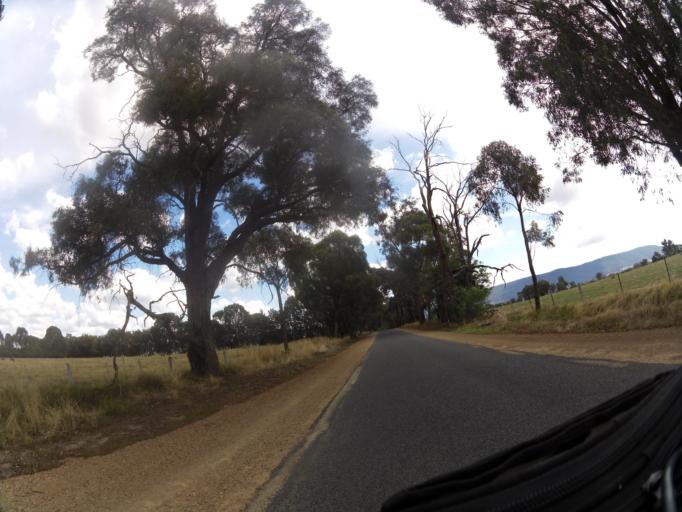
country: AU
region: Victoria
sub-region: Benalla
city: Benalla
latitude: -36.7488
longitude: 145.9914
